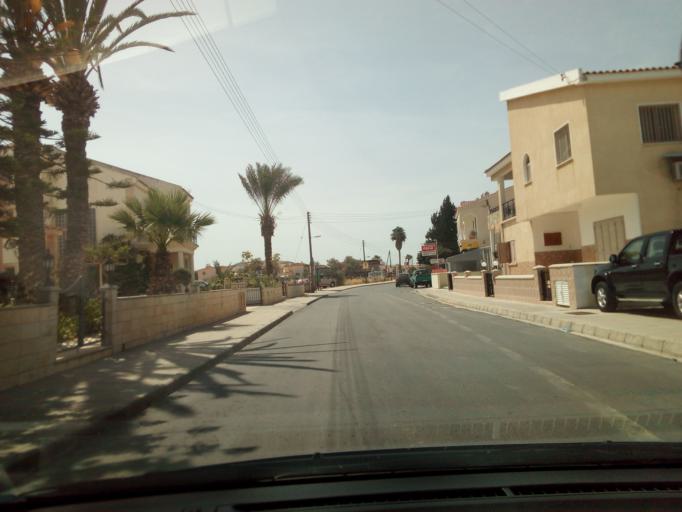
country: CY
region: Larnaka
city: Athienou
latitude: 35.0593
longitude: 33.5372
